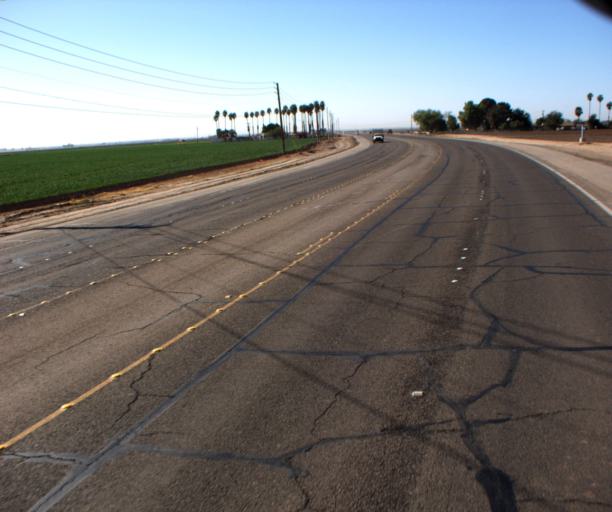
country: US
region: Arizona
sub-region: Yuma County
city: Somerton
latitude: 32.5927
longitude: -114.7695
